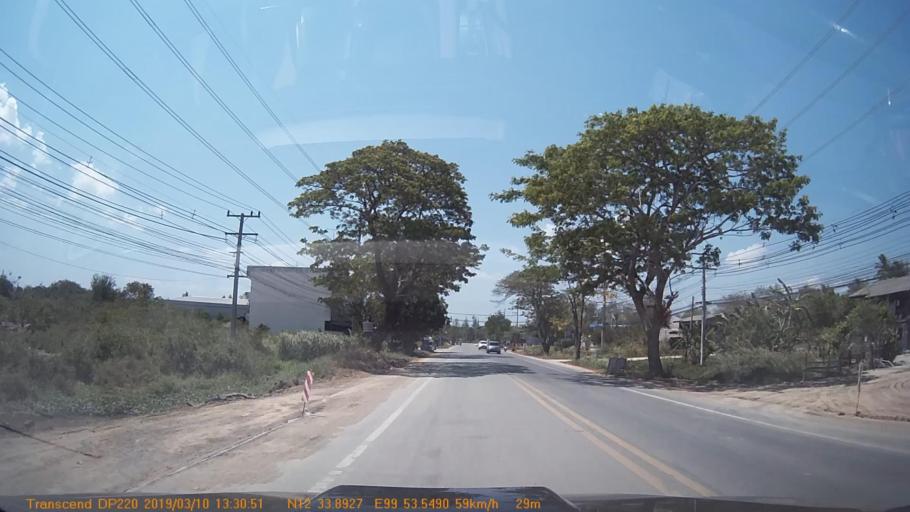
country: TH
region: Prachuap Khiri Khan
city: Hua Hin
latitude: 12.5650
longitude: 99.8920
